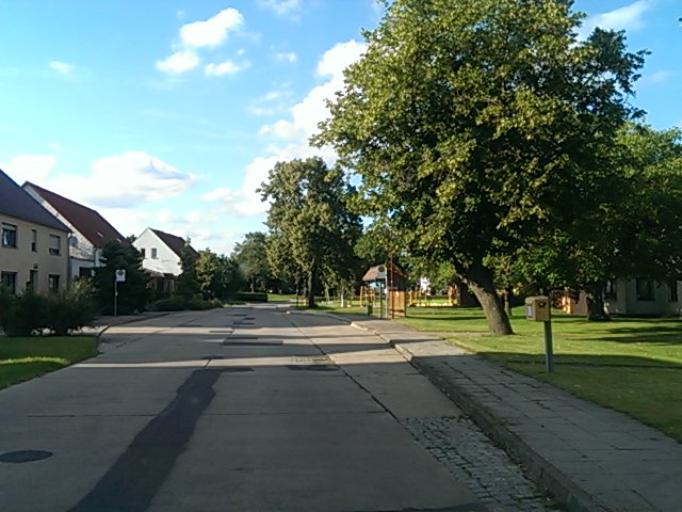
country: DE
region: Brandenburg
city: Niemegk
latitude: 52.0264
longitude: 12.6811
